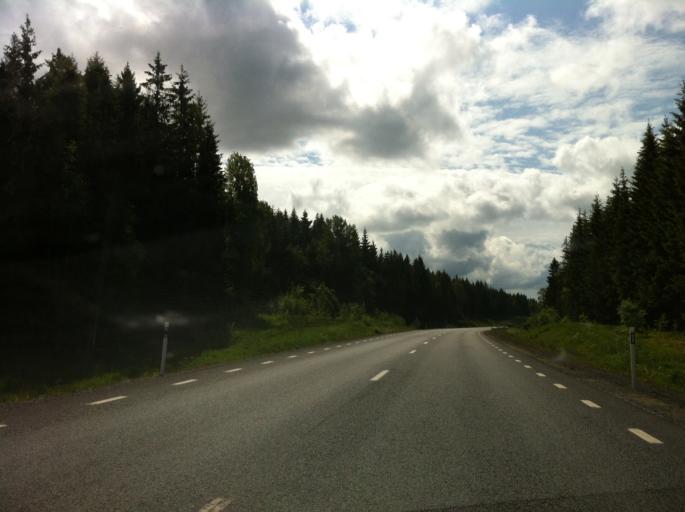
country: SE
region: Vaermland
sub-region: Karlstads Kommun
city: Edsvalla
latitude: 59.5690
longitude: 13.1809
